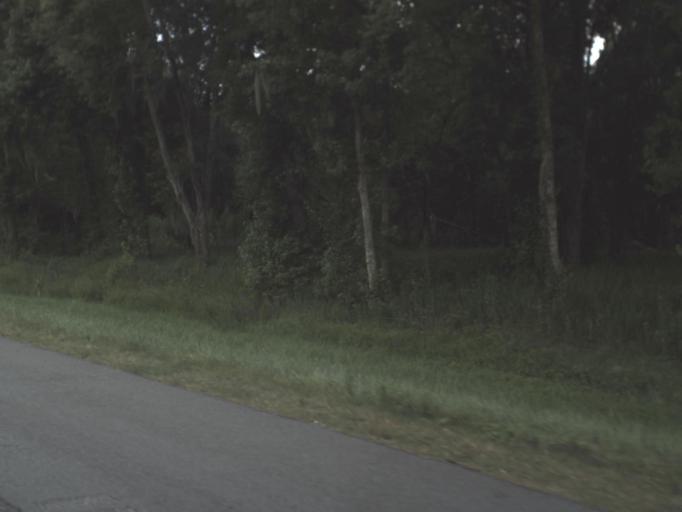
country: US
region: Florida
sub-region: Hamilton County
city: Jasper
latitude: 30.3953
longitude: -82.8808
